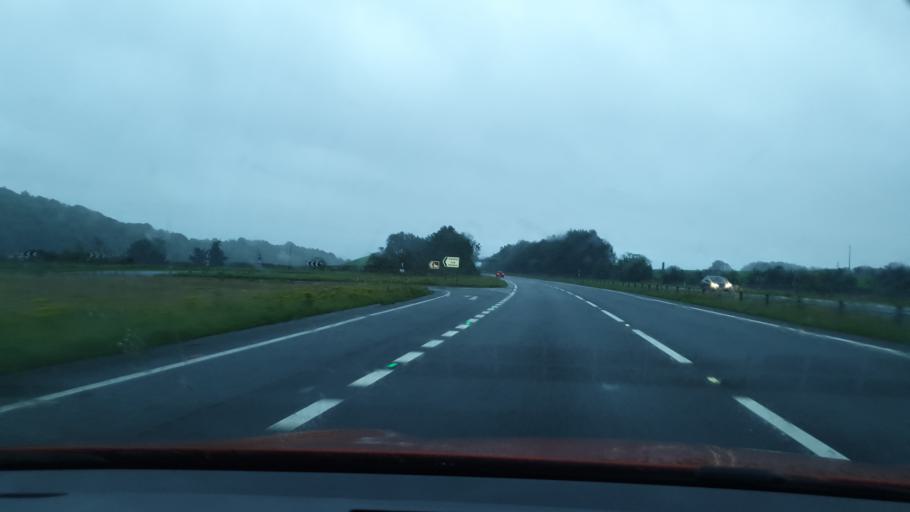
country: GB
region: England
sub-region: Cumbria
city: Grange-over-Sands
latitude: 54.2284
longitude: -2.9130
